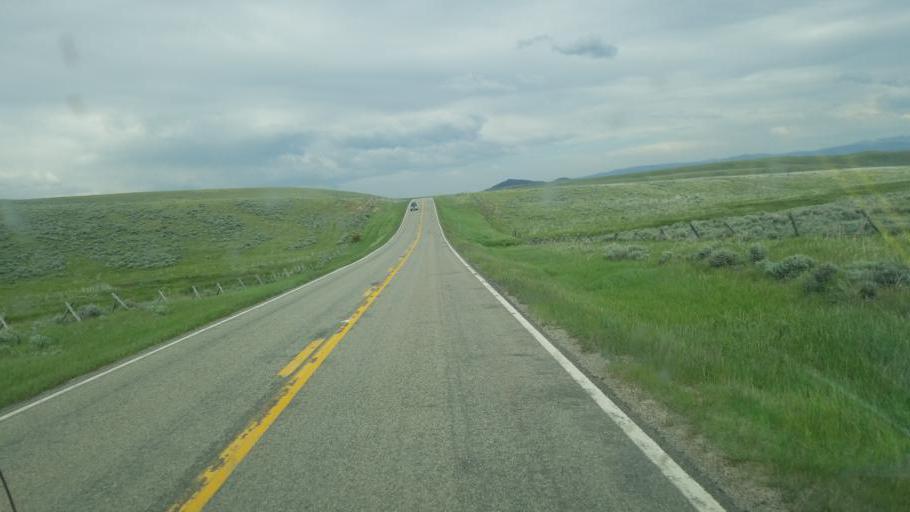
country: US
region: Montana
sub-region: Meagher County
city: White Sulphur Springs
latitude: 46.3544
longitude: -111.0338
